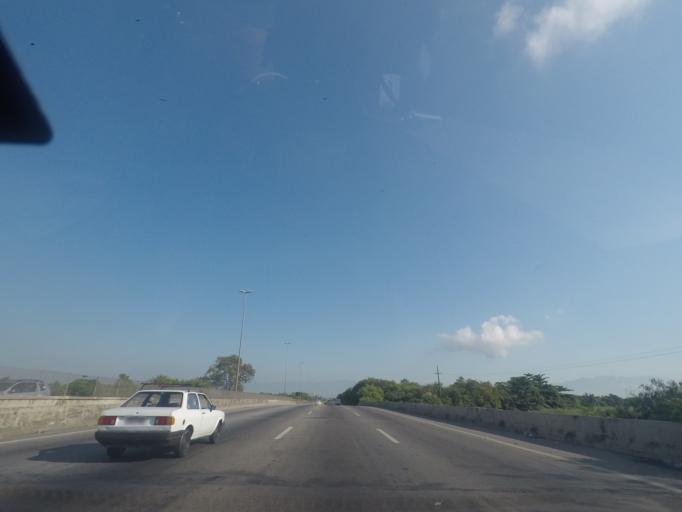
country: BR
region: Rio de Janeiro
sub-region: Duque De Caxias
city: Duque de Caxias
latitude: -22.7467
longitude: -43.2878
